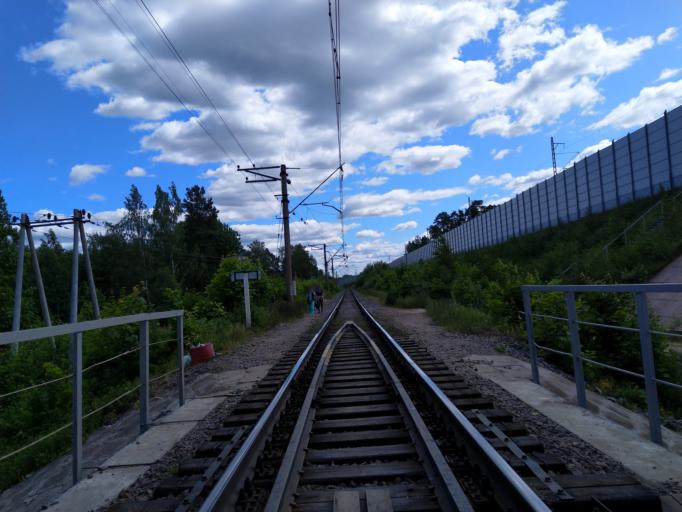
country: RU
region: Leningrad
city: Sapernoye
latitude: 60.6818
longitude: 30.0096
